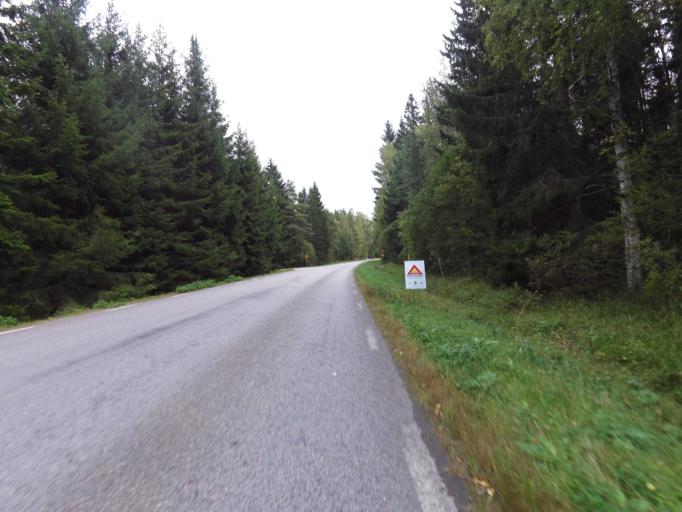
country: SE
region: Gaevleborg
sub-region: Gavle Kommun
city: Valbo
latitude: 60.6608
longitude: 16.9702
